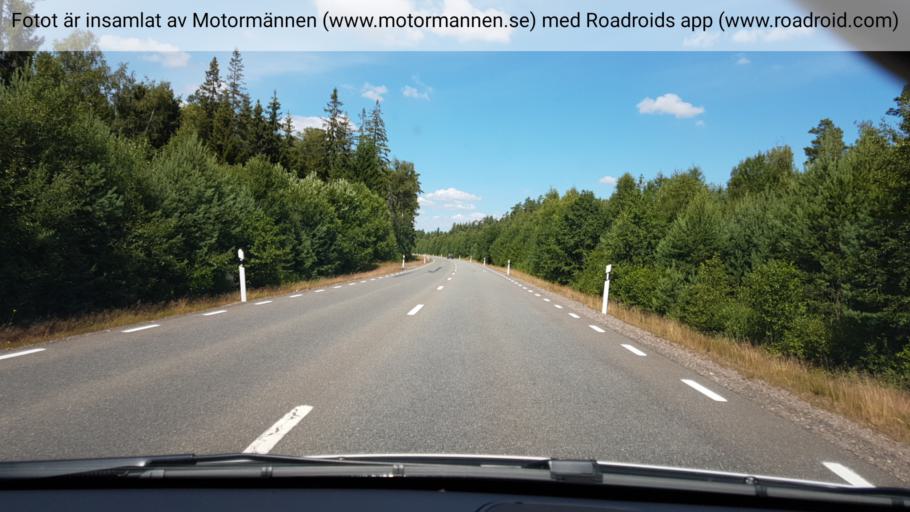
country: SE
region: Vaestra Goetaland
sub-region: Tibro Kommun
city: Tibro
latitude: 58.5485
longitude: 14.1417
